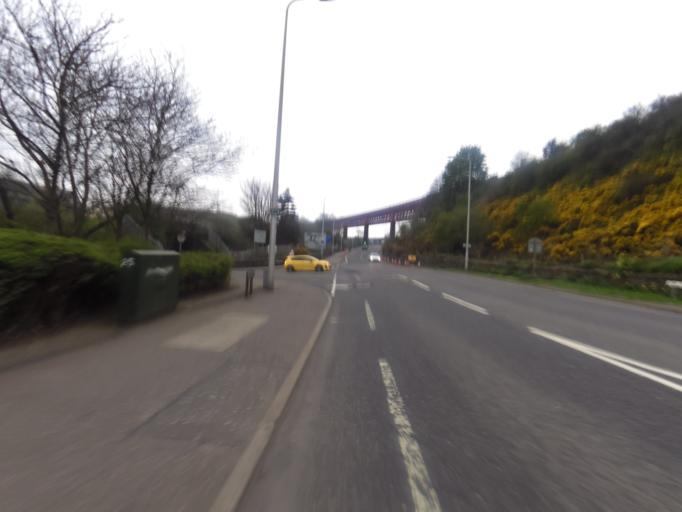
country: GB
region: Scotland
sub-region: Fife
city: Inverkeithing
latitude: 56.0239
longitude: -3.4041
